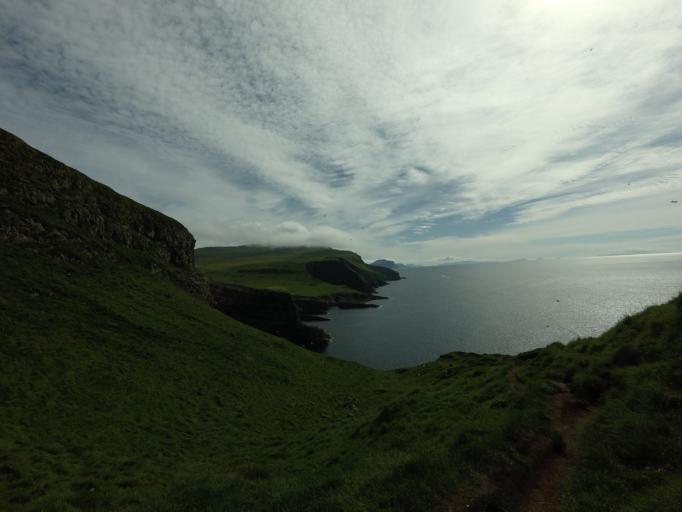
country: FO
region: Vagar
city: Sorvagur
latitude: 62.1020
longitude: -7.6612
